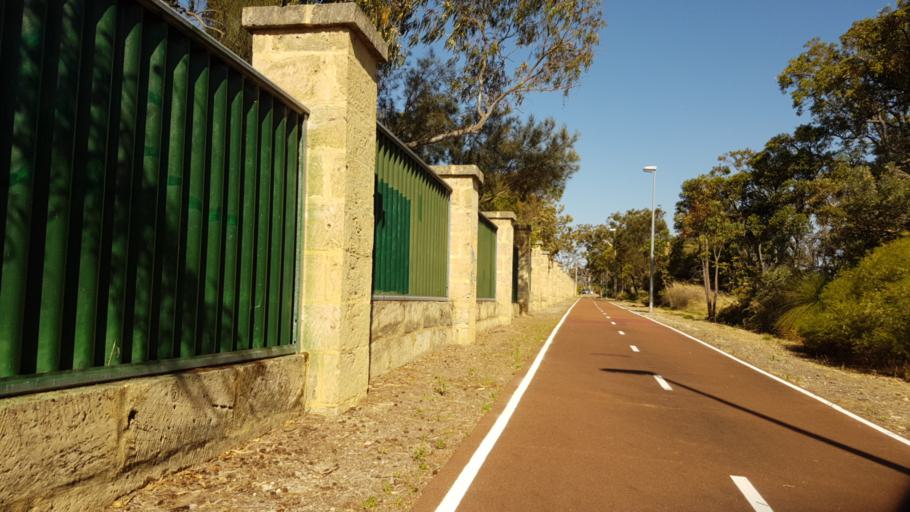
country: AU
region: Western Australia
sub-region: Stirling
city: Balcatta
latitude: -31.8563
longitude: 115.8108
